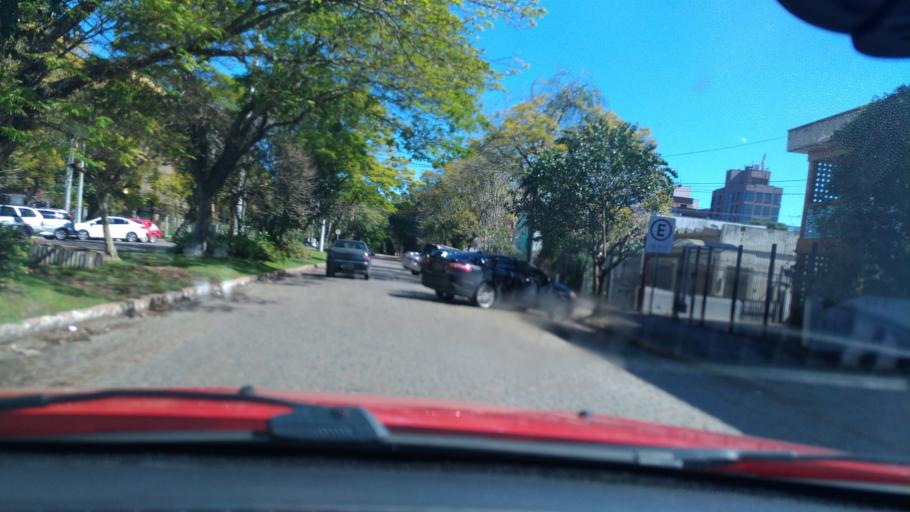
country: BR
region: Rio Grande do Sul
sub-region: Porto Alegre
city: Porto Alegre
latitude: -30.0450
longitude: -51.2025
